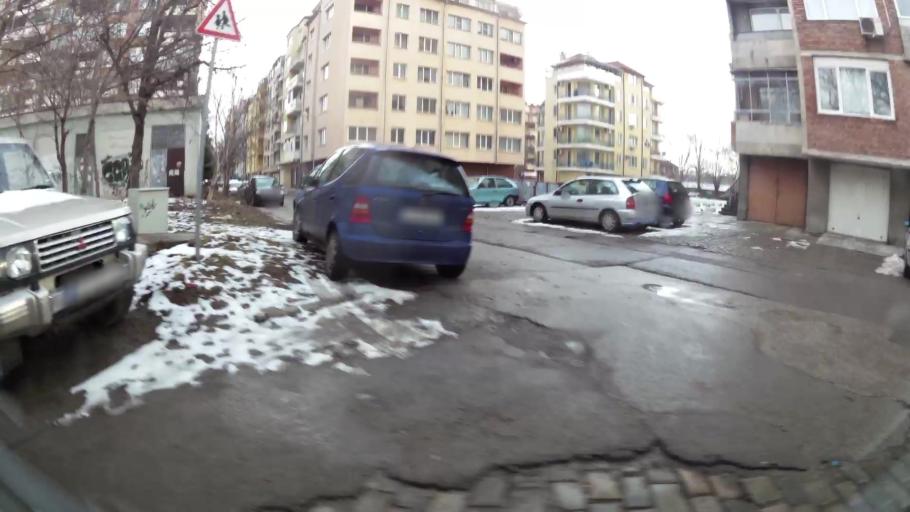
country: BG
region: Sofia-Capital
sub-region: Stolichna Obshtina
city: Sofia
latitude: 42.6991
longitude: 23.2940
